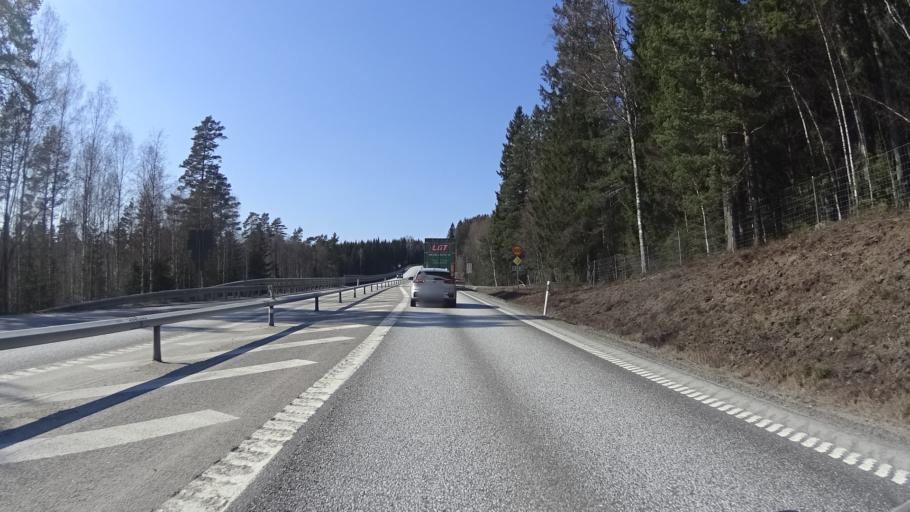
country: SE
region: OErebro
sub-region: Karlskoga Kommun
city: Karlskoga
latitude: 59.2965
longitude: 14.6550
